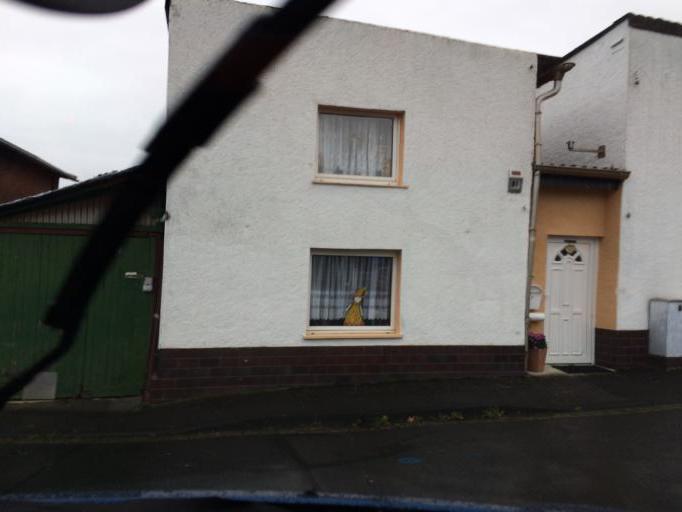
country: DE
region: North Rhine-Westphalia
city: Bruhl
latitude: 50.7747
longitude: 6.9134
